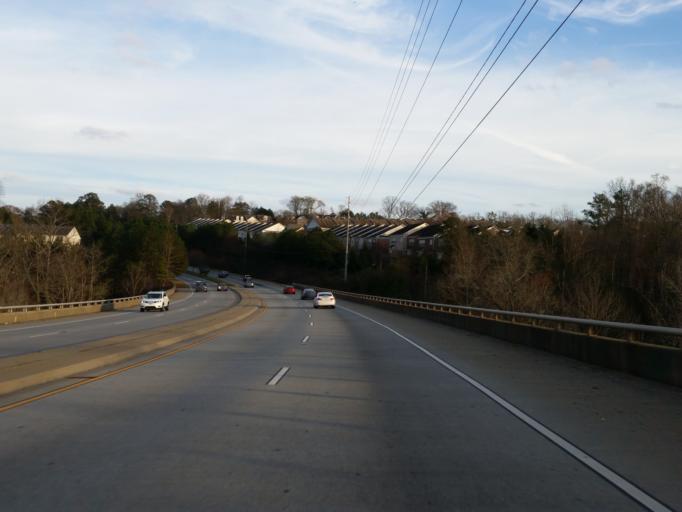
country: US
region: Georgia
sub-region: Cobb County
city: Smyrna
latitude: 33.8386
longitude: -84.5152
